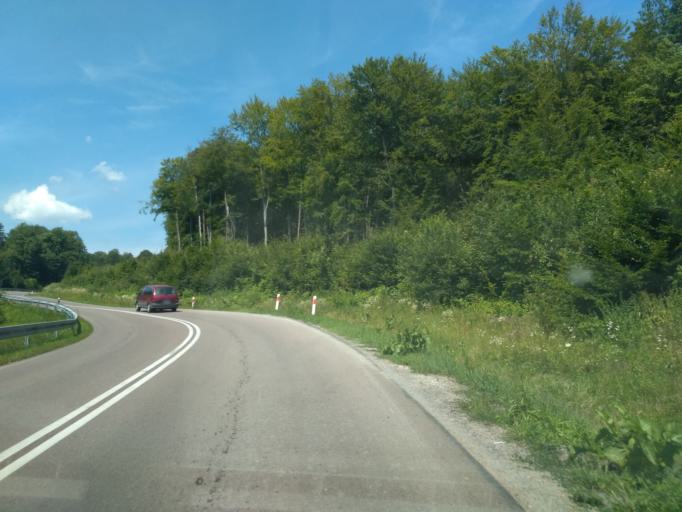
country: PL
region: Subcarpathian Voivodeship
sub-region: Powiat przemyski
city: Krasiczyn
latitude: 49.7871
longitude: 22.6187
